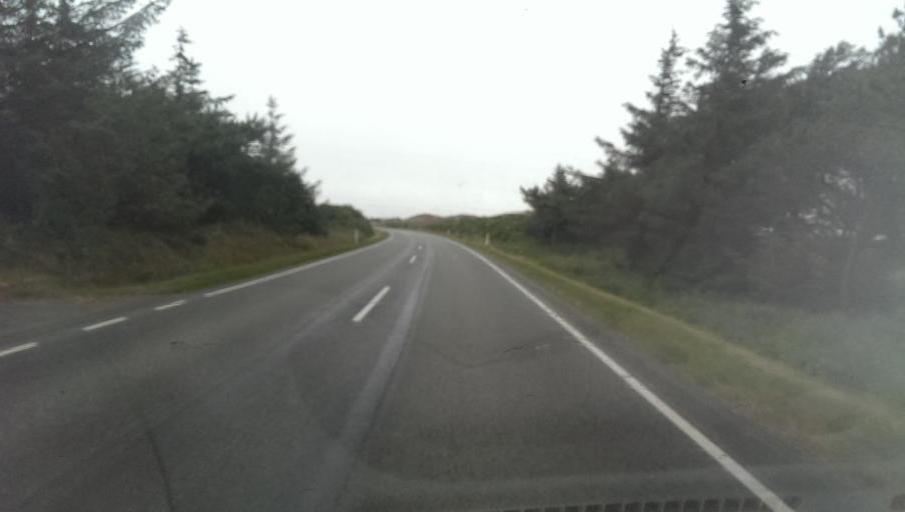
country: DK
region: Central Jutland
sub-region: Ringkobing-Skjern Kommune
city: Hvide Sande
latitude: 55.9431
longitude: 8.1567
